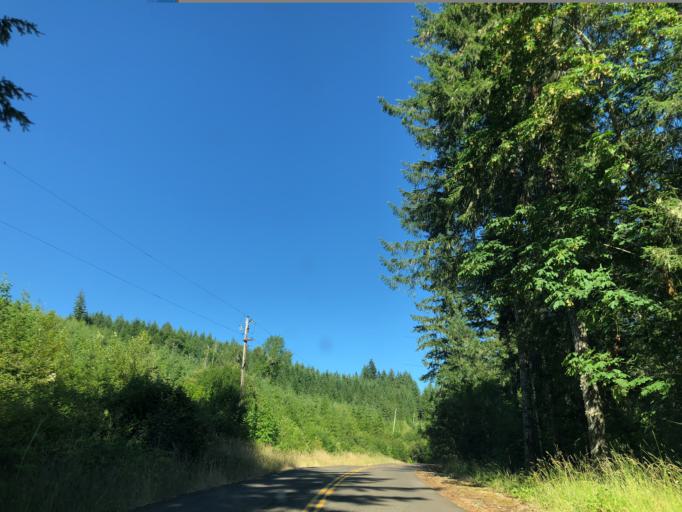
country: US
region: Oregon
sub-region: Linn County
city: Sweet Home
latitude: 44.4654
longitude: -122.6868
